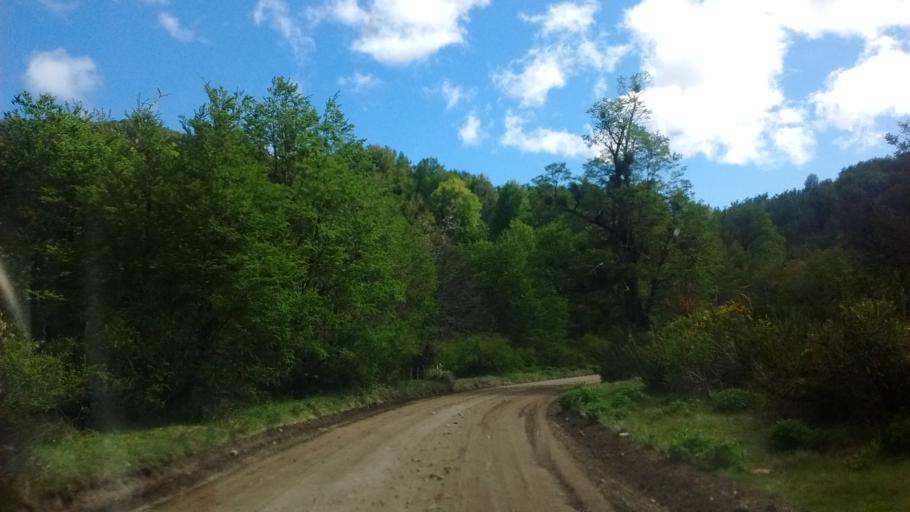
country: AR
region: Neuquen
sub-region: Departamento de Lacar
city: San Martin de los Andes
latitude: -40.3640
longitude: -71.4768
